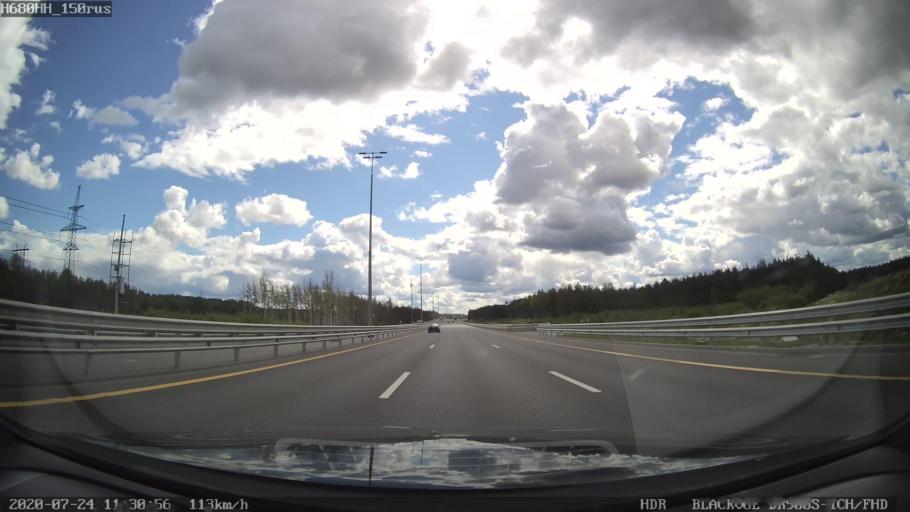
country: RU
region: Leningrad
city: Krasnyy Bor
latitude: 59.6637
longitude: 30.6229
